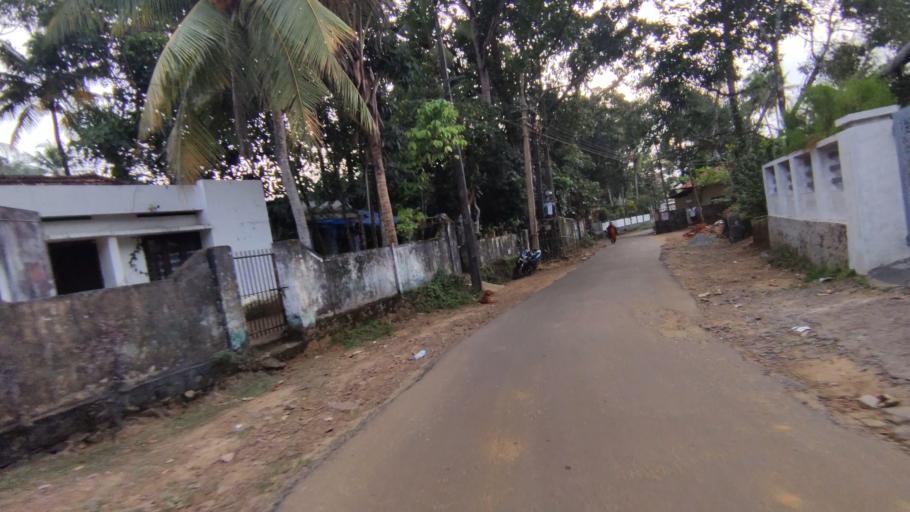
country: IN
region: Kerala
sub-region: Kottayam
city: Kottayam
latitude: 9.6343
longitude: 76.5027
